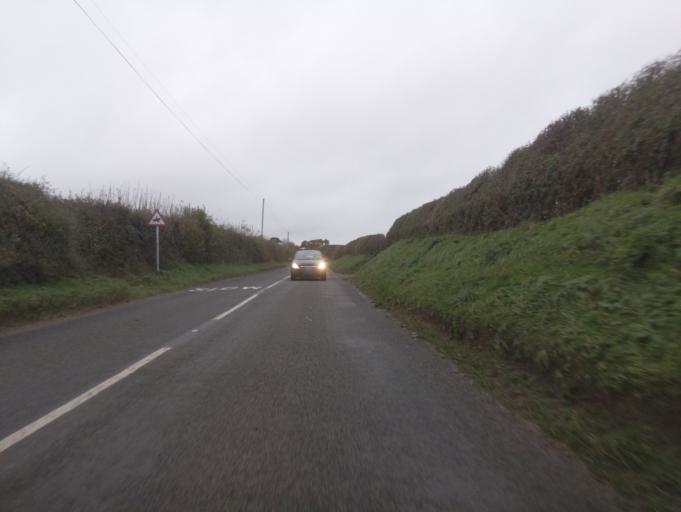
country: GB
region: England
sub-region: Dorset
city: Sherborne
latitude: 50.9605
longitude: -2.5440
